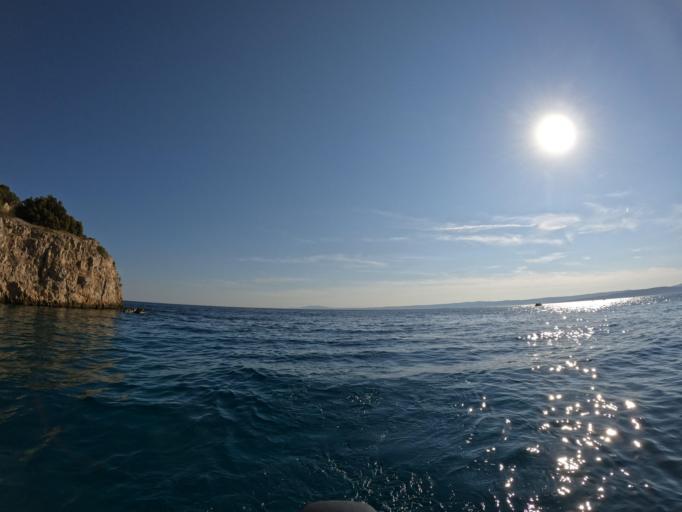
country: HR
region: Primorsko-Goranska
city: Punat
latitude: 44.9726
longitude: 14.6352
